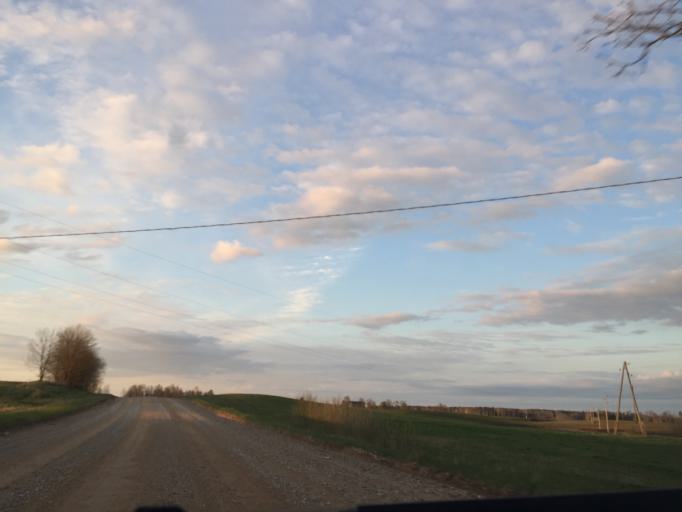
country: LV
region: Gulbenes Rajons
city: Gulbene
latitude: 57.2033
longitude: 26.7772
